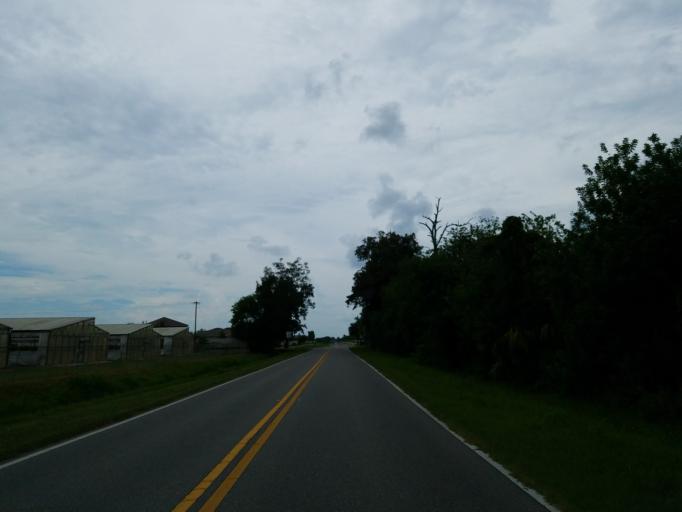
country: US
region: Florida
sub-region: Hillsborough County
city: Ruskin
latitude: 27.7279
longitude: -82.4379
